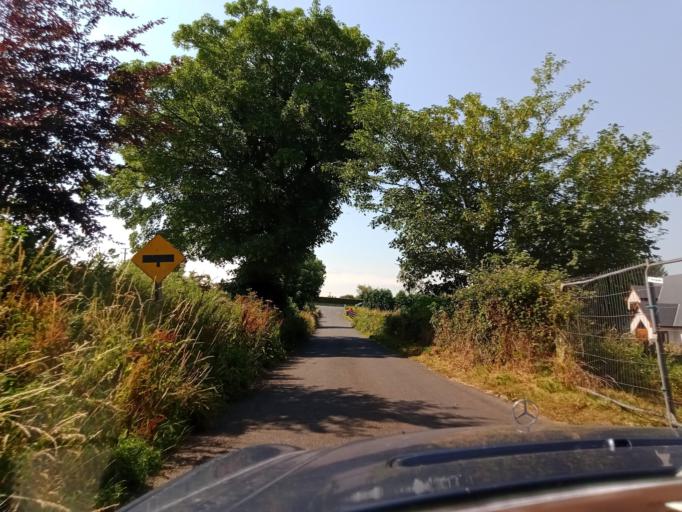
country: IE
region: Leinster
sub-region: Kilkenny
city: Piltown
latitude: 52.3420
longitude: -7.3179
